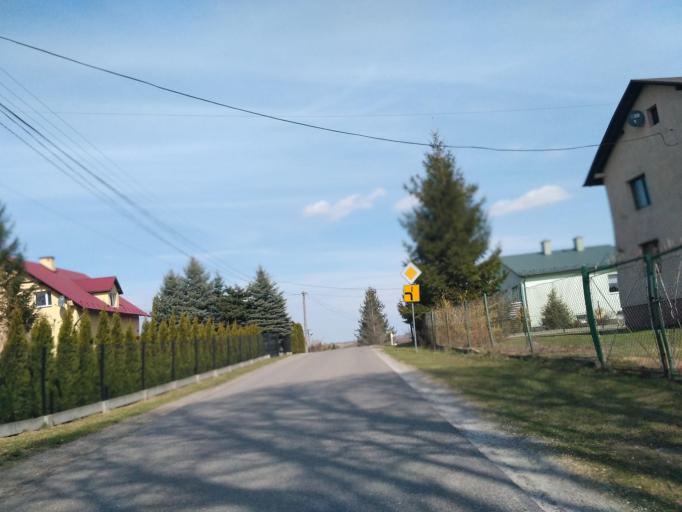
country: PL
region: Subcarpathian Voivodeship
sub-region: Powiat rzeszowski
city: Zglobien
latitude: 50.0156
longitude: 21.8563
